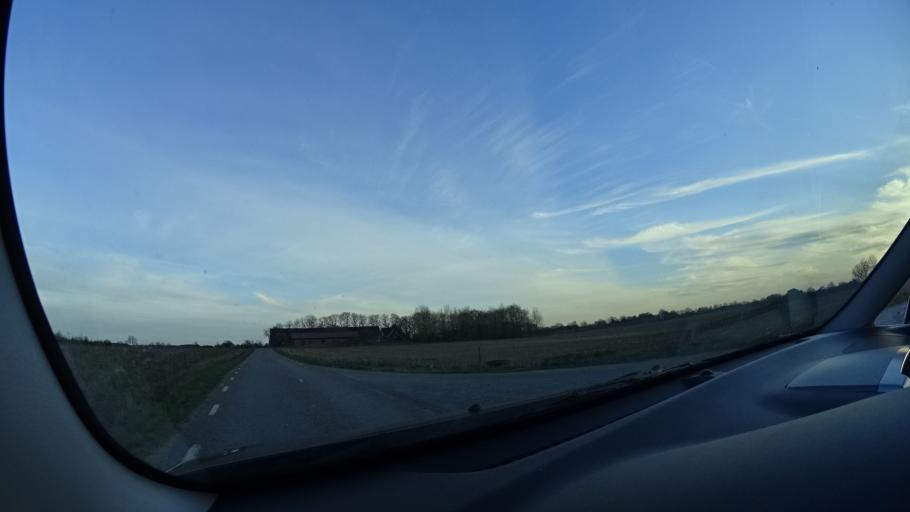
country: SE
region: Skane
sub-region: Eslovs Kommun
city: Stehag
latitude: 55.8734
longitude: 13.4443
